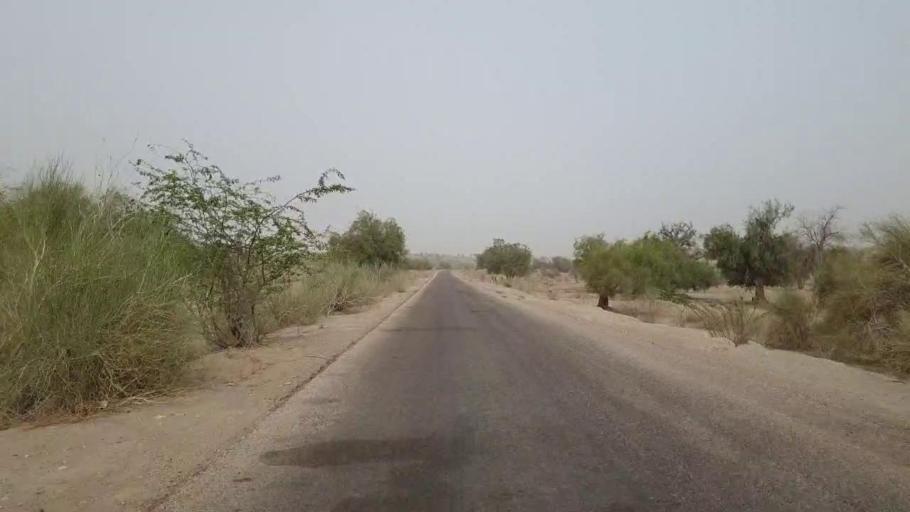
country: PK
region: Sindh
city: Islamkot
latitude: 24.5913
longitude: 70.2853
